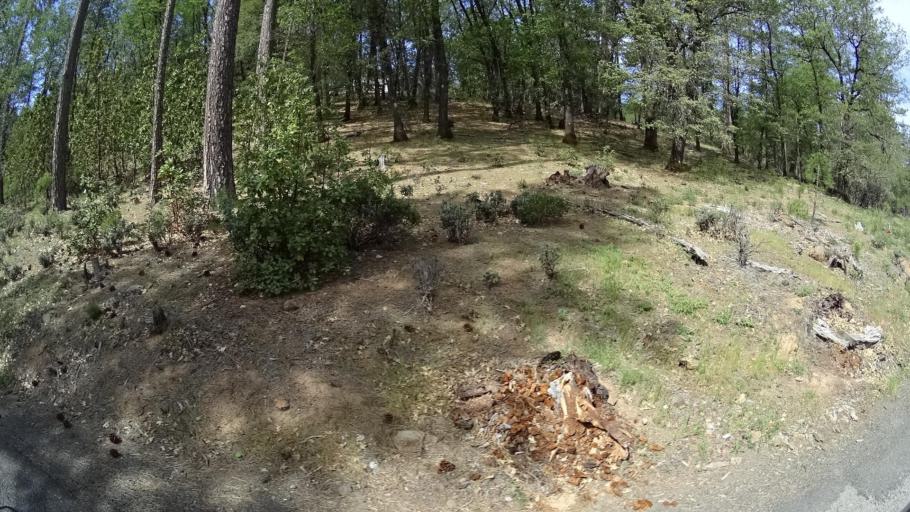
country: US
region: California
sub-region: Lake County
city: Cobb
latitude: 38.8903
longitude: -122.7836
